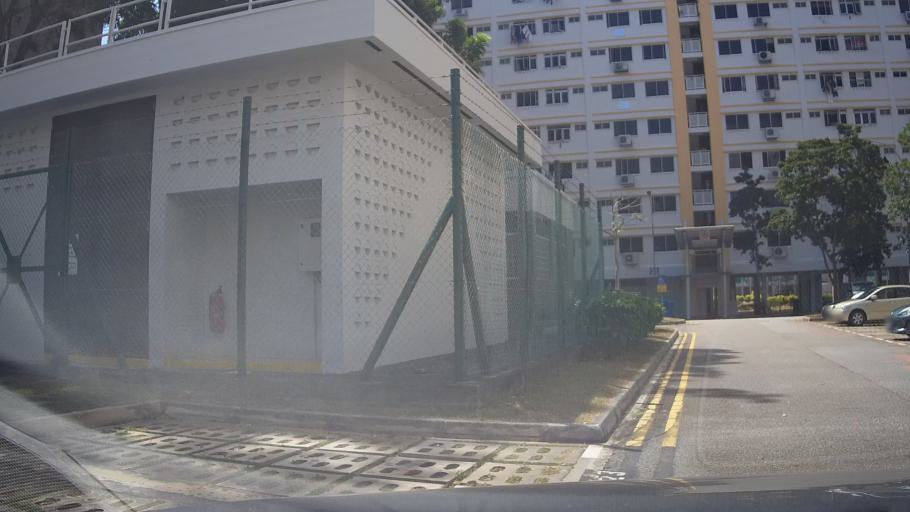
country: MY
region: Johor
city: Kampung Pasir Gudang Baru
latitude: 1.3702
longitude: 103.9549
